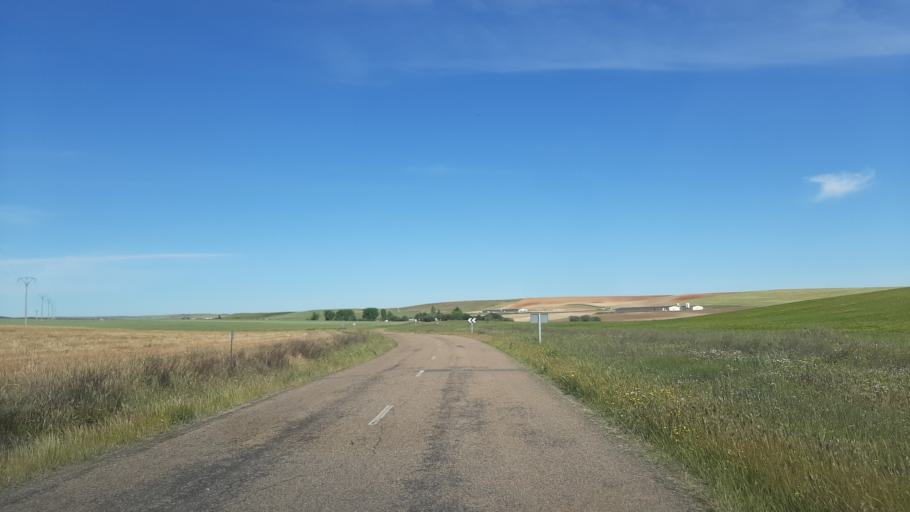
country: ES
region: Castille and Leon
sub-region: Provincia de Salamanca
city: Aldeaseca de Alba
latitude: 40.8188
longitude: -5.4708
